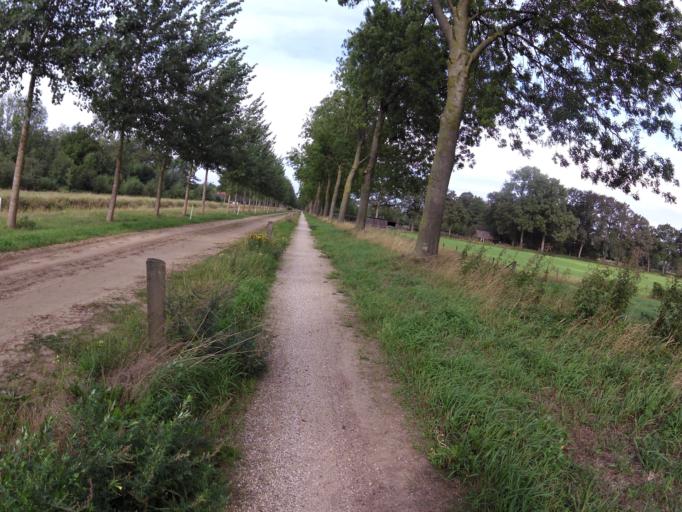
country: NL
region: Gelderland
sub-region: Oude IJsselstreek
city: Varsseveld
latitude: 51.9456
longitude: 6.4927
